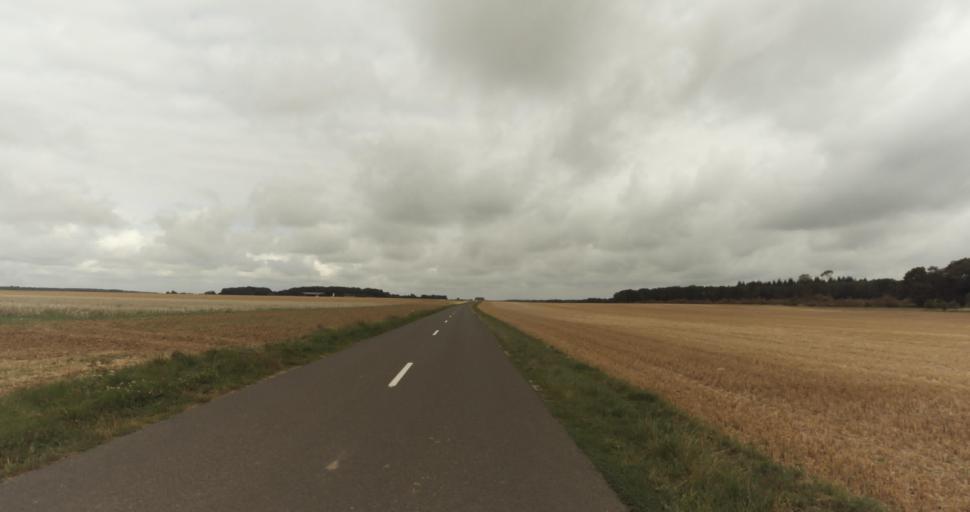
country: FR
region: Haute-Normandie
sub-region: Departement de l'Eure
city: Pacy-sur-Eure
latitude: 48.9538
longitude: 1.3501
